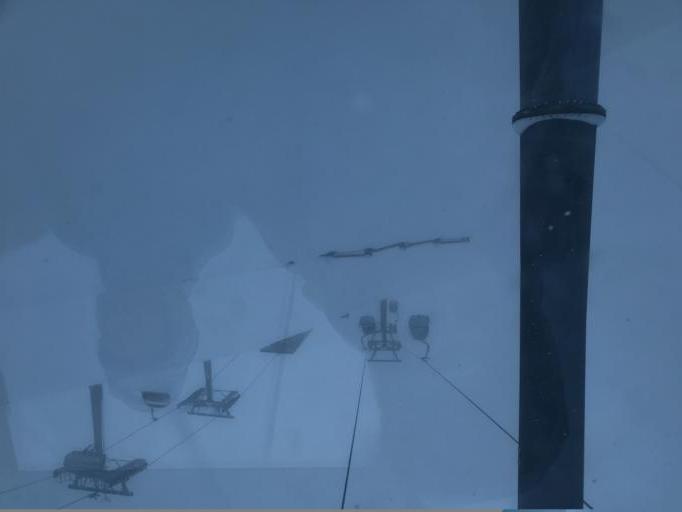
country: AT
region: Salzburg
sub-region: Politischer Bezirk Zell am See
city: Viehhofen
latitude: 47.3231
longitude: 12.7379
